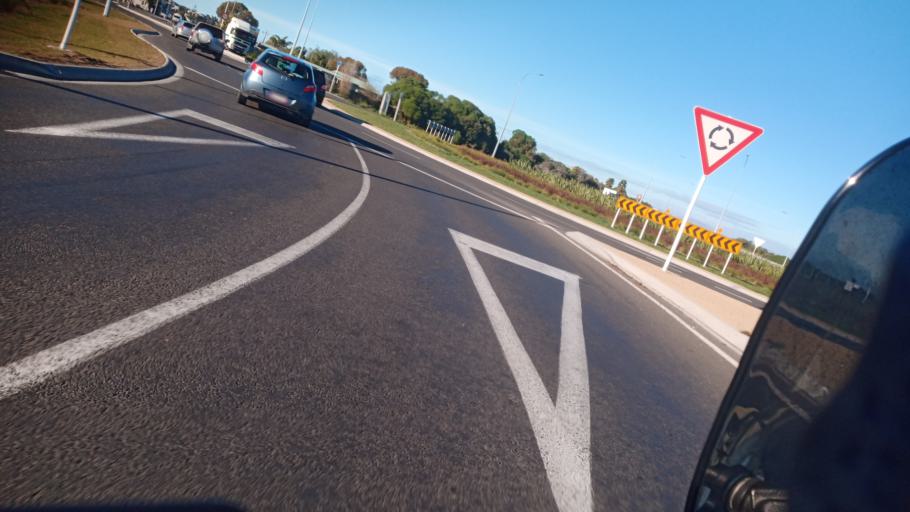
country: NZ
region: Hawke's Bay
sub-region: Napier City
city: Napier
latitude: -39.4743
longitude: 176.8772
